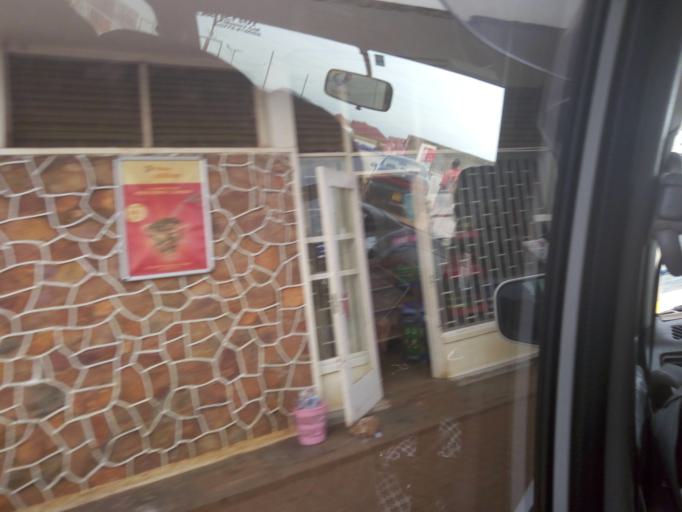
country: UG
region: Western Region
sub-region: Masindi District
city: Masindi
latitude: 1.6840
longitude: 31.7213
